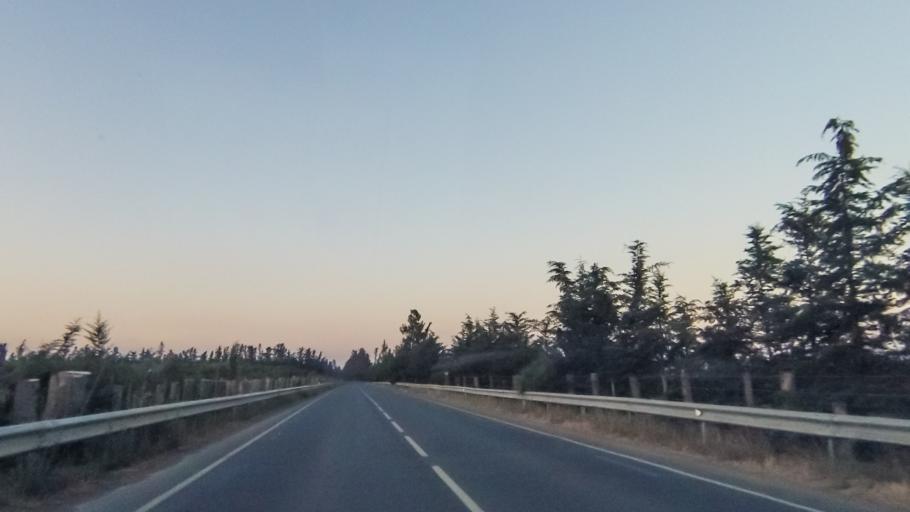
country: CY
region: Limassol
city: Ypsonas
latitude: 34.6487
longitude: 32.9796
